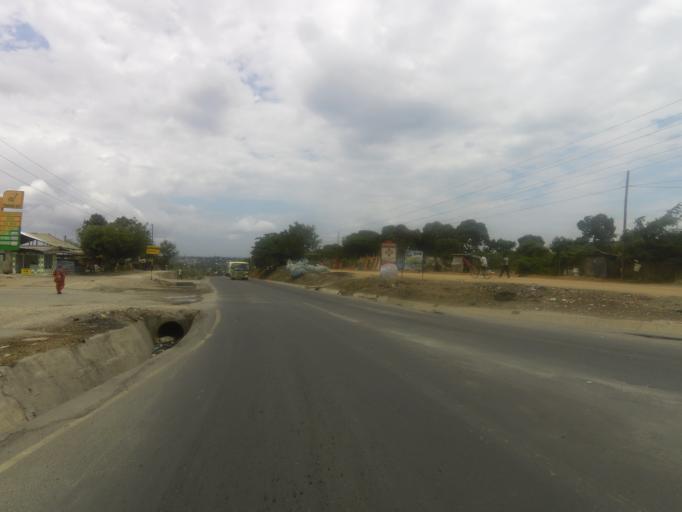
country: TZ
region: Pwani
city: Vikindu
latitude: -6.9297
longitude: 39.2720
